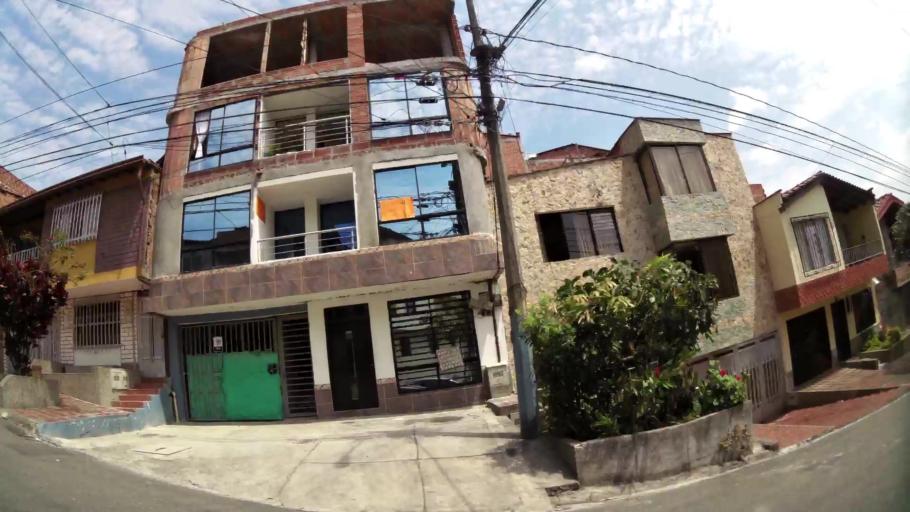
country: CO
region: Antioquia
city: Bello
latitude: 6.3158
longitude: -75.5660
